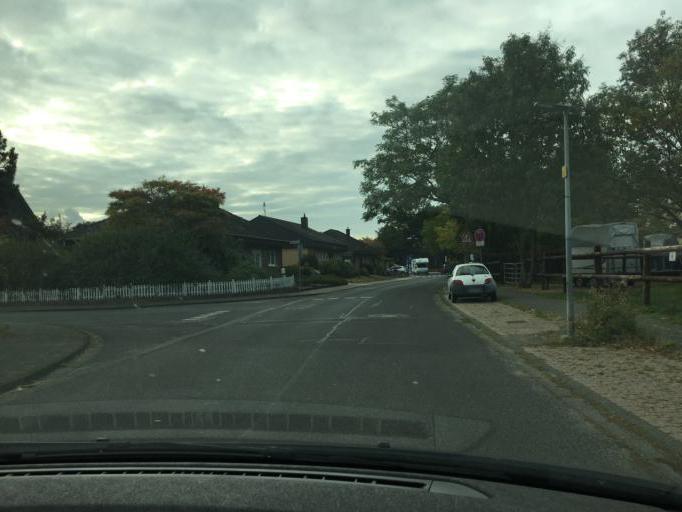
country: DE
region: North Rhine-Westphalia
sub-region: Regierungsbezirk Koln
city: Merzenich
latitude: 50.8558
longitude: 6.5836
